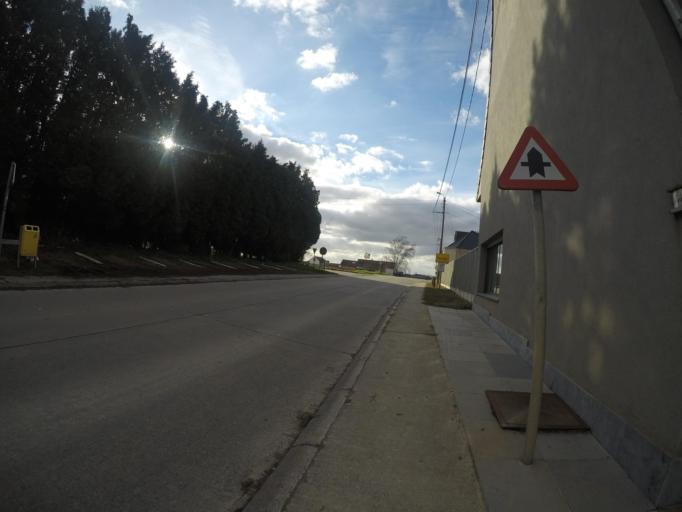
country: BE
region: Flanders
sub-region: Provincie Vlaams-Brabant
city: Pepingen
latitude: 50.7266
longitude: 4.1407
